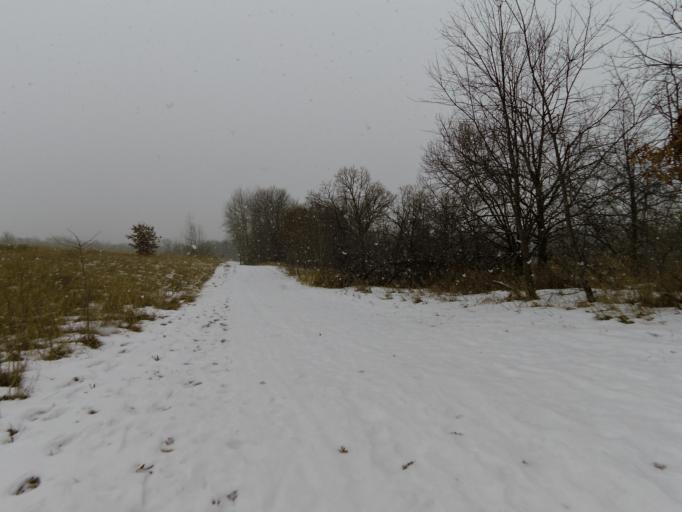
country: US
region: Minnesota
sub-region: Washington County
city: Lake Elmo
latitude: 44.9802
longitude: -92.9072
